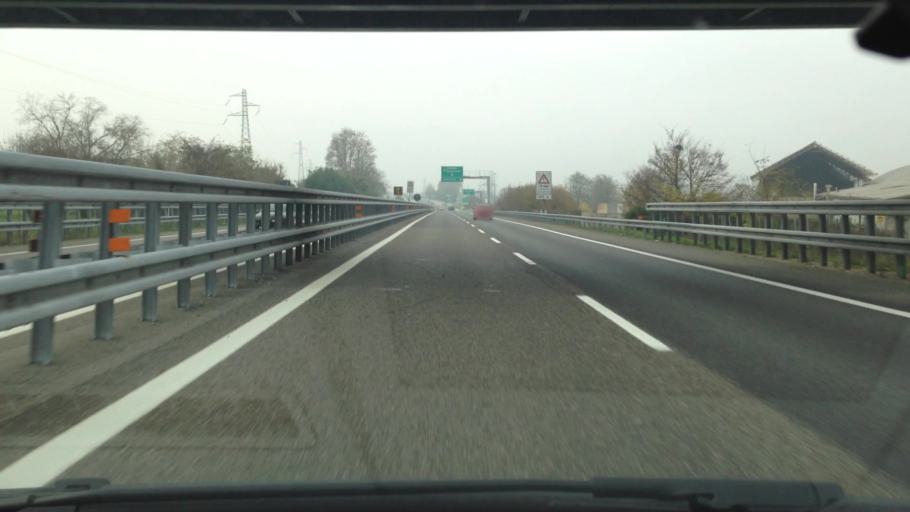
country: IT
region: Piedmont
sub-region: Provincia di Torino
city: Cambiano
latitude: 44.9596
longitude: 7.7922
